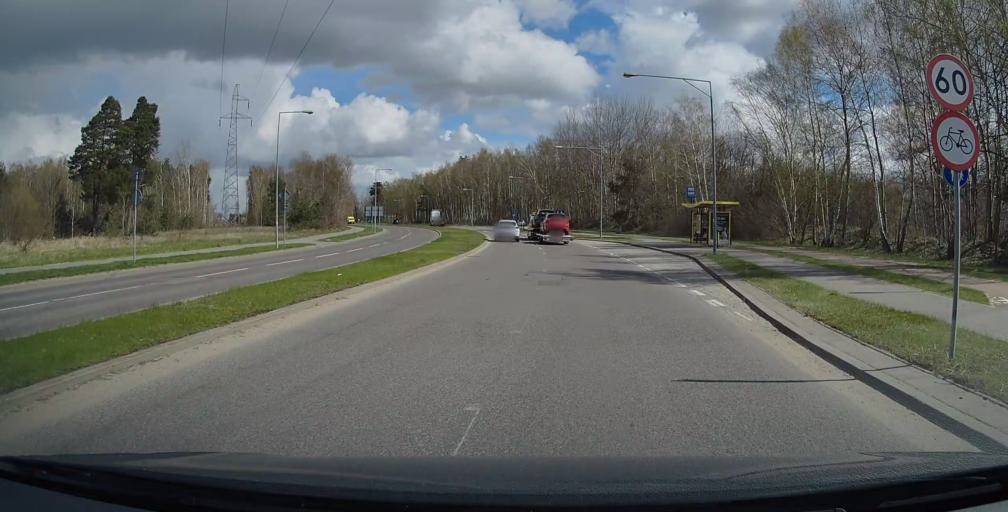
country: PL
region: Masovian Voivodeship
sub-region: Ostroleka
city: Ostroleka
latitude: 53.0621
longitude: 21.5839
